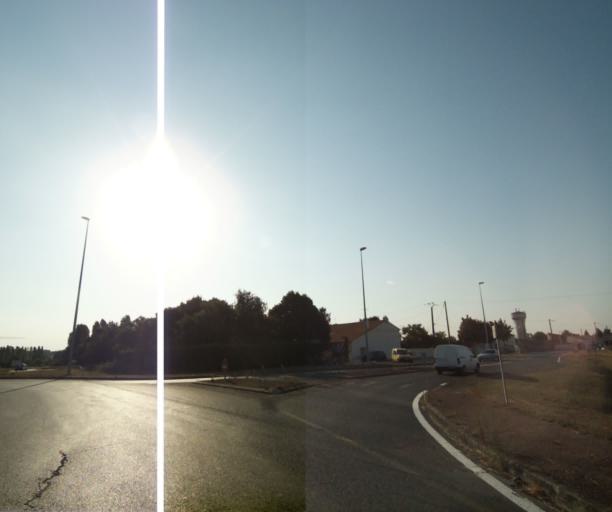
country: FR
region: Poitou-Charentes
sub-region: Departement de la Charente-Maritime
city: Tonnay-Charente
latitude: 45.9531
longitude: -0.8787
